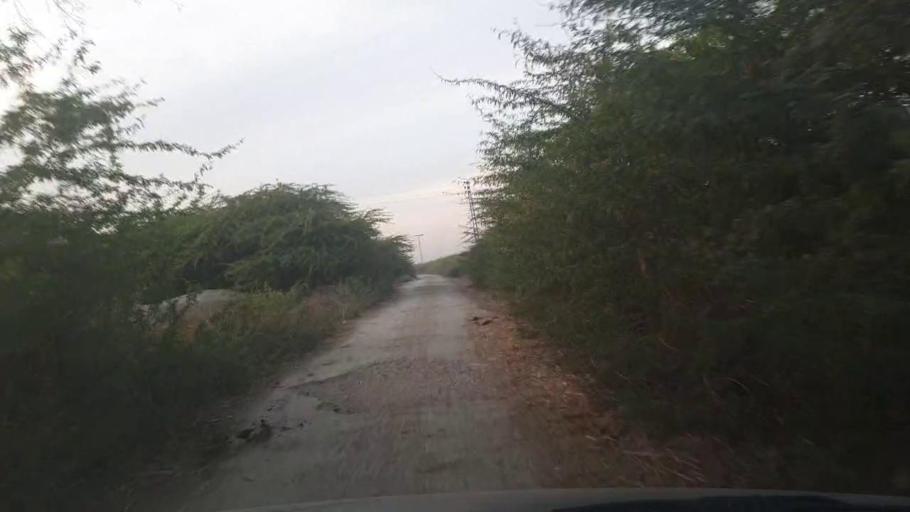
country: PK
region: Sindh
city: Kunri
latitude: 25.2272
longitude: 69.5356
